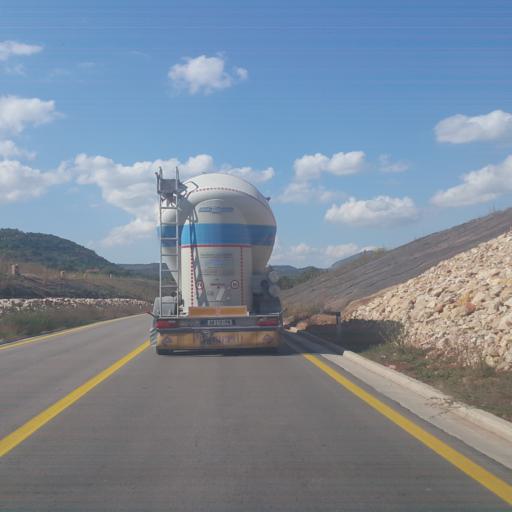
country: RS
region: Central Serbia
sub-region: Pirotski Okrug
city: Bela Palanka
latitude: 43.2606
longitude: 22.2558
